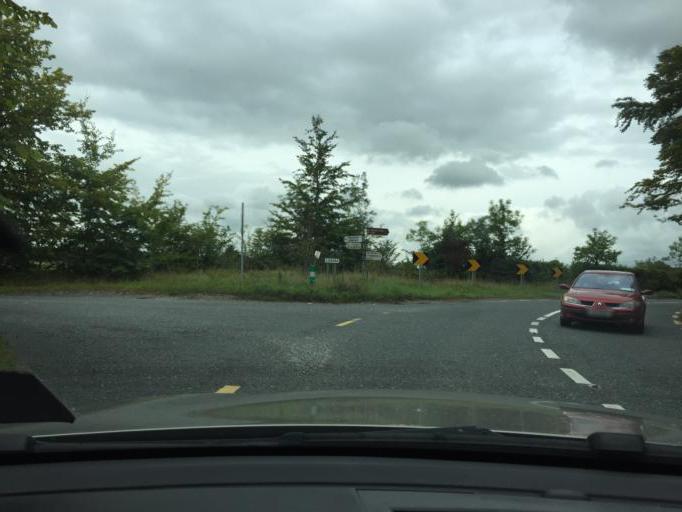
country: IE
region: Leinster
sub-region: Kildare
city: Maynooth
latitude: 53.3927
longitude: -6.5756
